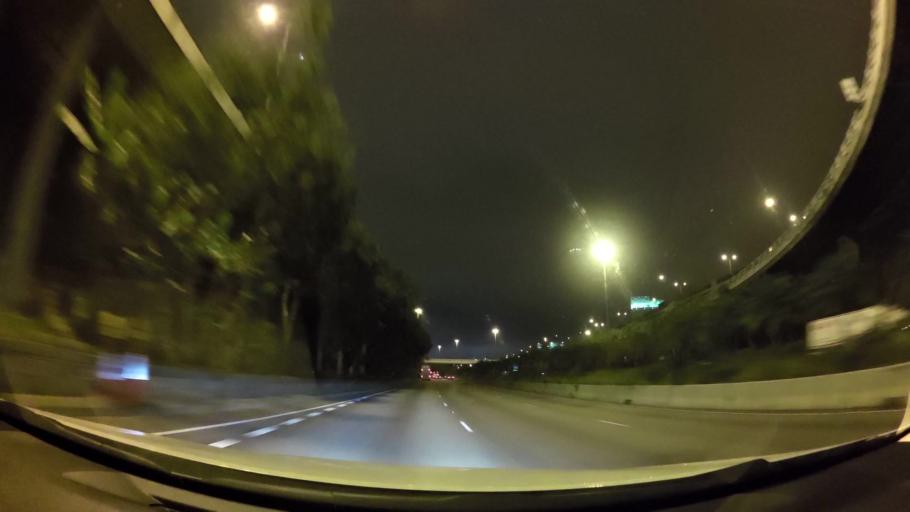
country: HK
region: Sham Shui Po
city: Sham Shui Po
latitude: 22.3420
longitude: 114.1313
